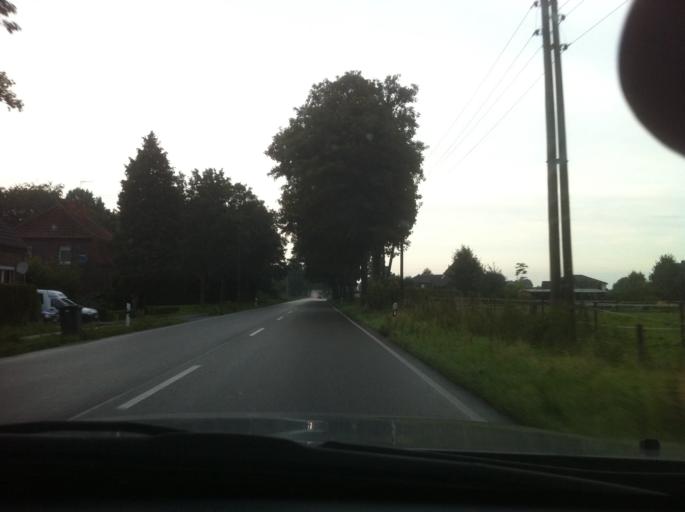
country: DE
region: North Rhine-Westphalia
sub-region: Regierungsbezirk Dusseldorf
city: Kleve
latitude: 51.7456
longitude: 6.1588
